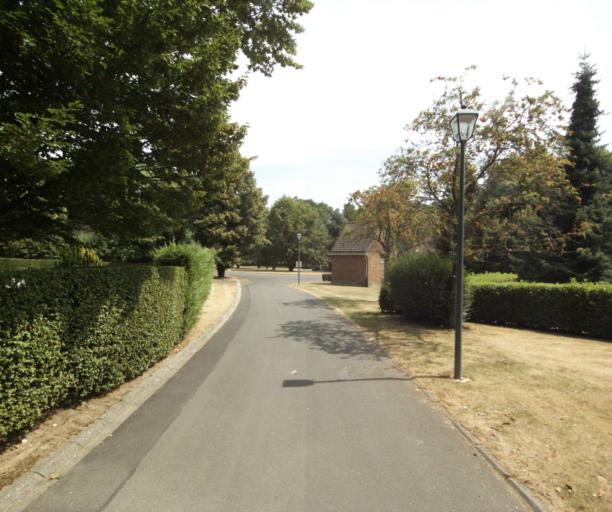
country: FR
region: Nord-Pas-de-Calais
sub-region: Departement du Nord
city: Mouvaux
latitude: 50.7239
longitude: 3.1220
